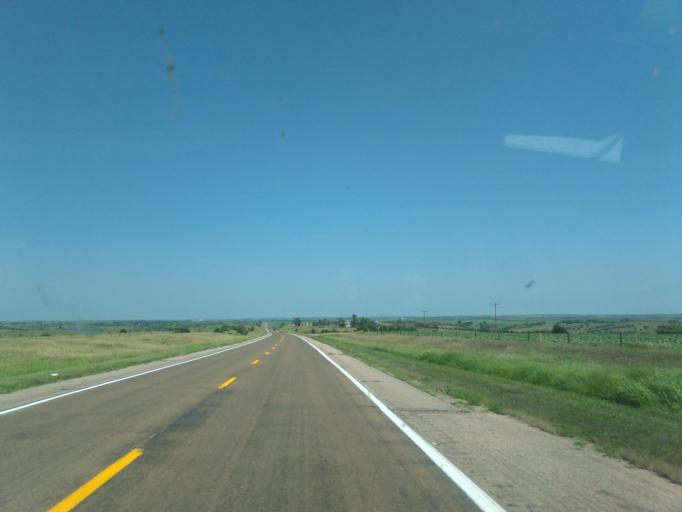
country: US
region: Nebraska
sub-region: Frontier County
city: Stockville
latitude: 40.6118
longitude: -100.6298
